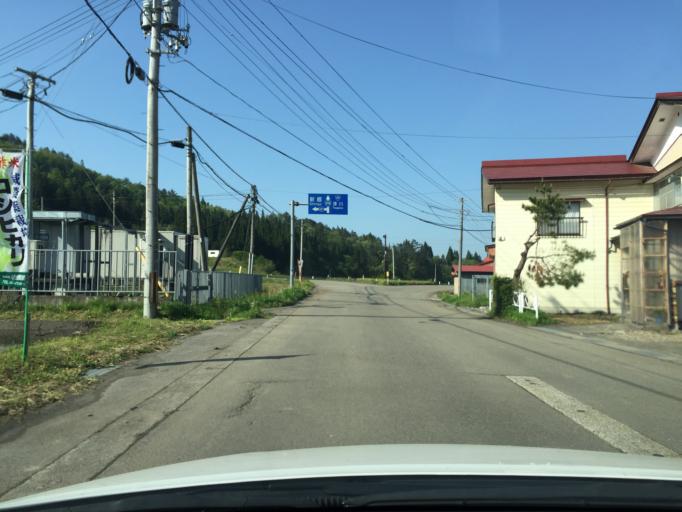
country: JP
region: Fukushima
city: Kitakata
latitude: 37.6815
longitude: 139.6581
